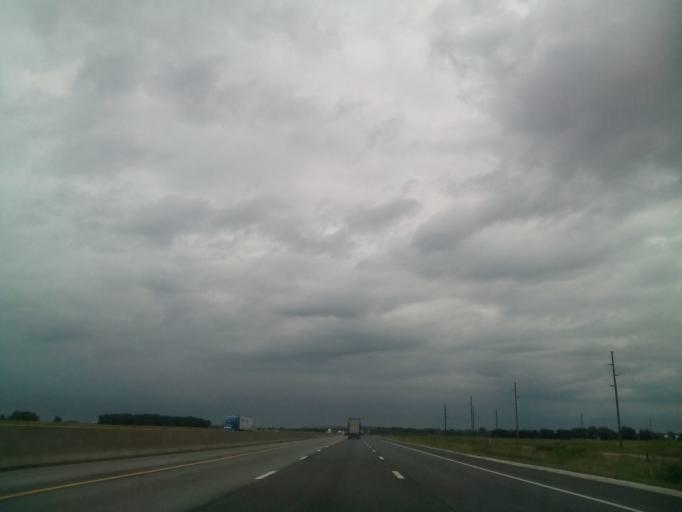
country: US
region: Ohio
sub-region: Sandusky County
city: Woodville
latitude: 41.4799
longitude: -83.3461
